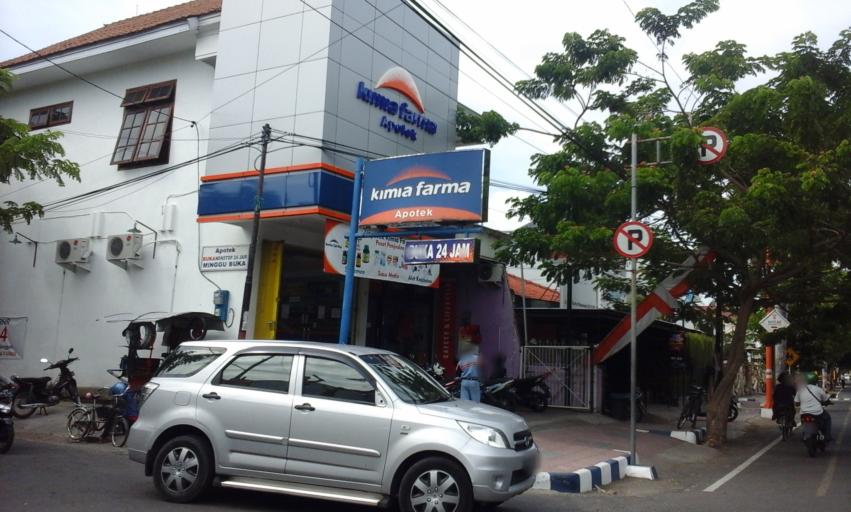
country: ID
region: East Java
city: Krajan
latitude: -8.2202
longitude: 114.3686
